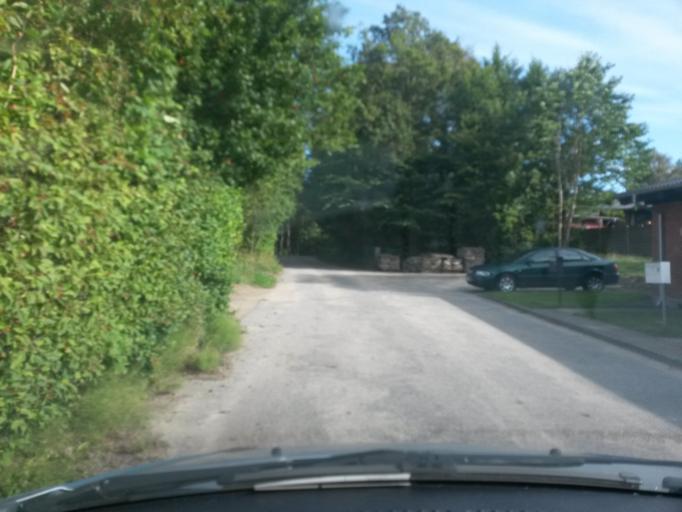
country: DK
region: Central Jutland
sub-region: Silkeborg Kommune
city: Kjellerup
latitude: 56.2879
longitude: 9.4386
